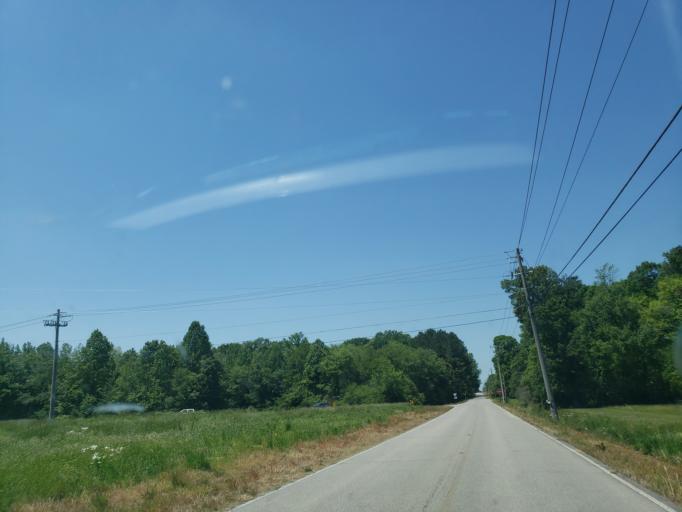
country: US
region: Alabama
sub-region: Madison County
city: Harvest
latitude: 34.9625
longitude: -86.7116
